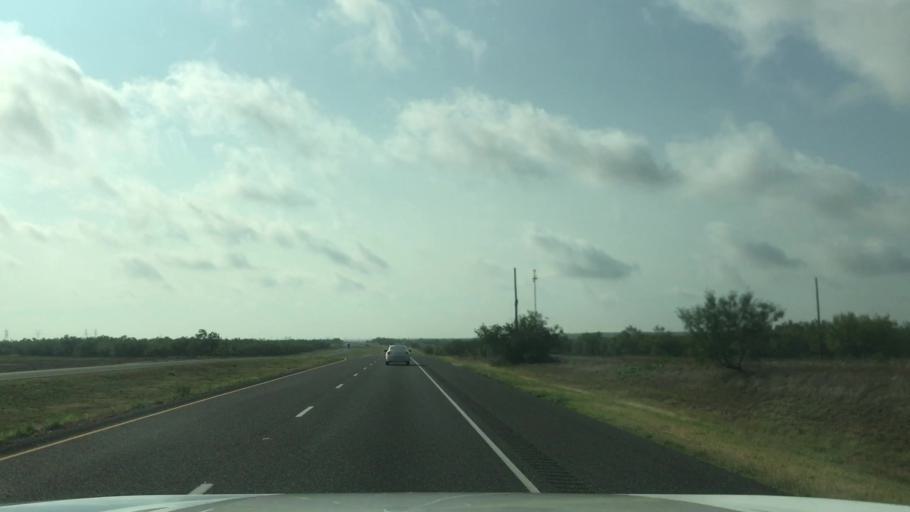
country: US
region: Texas
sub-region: Scurry County
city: Snyder
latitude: 32.8644
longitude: -101.0301
